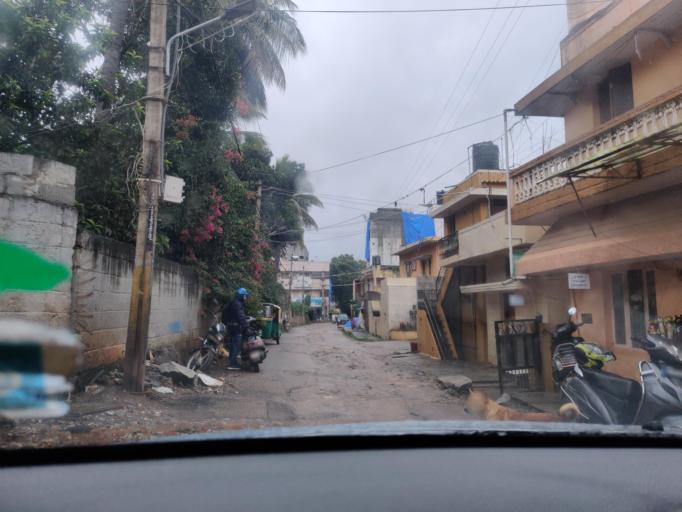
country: IN
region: Karnataka
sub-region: Bangalore Urban
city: Bangalore
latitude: 13.0298
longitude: 77.6390
